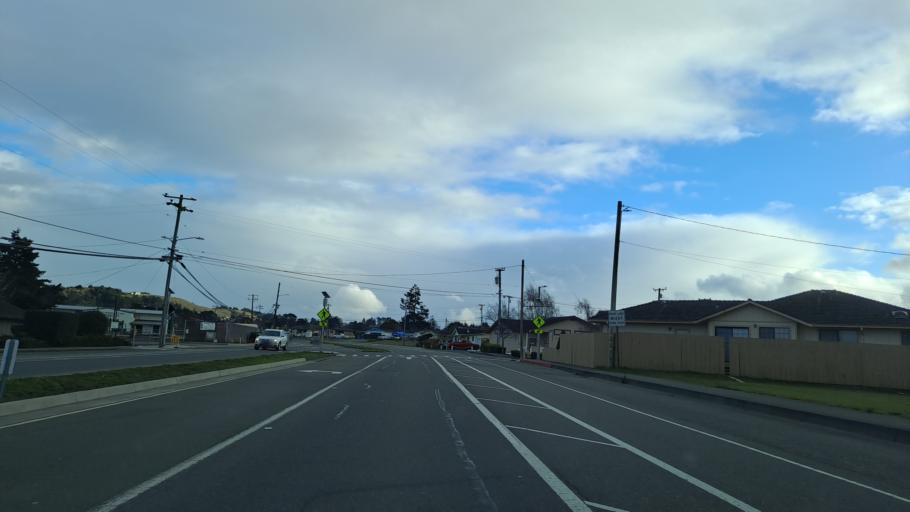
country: US
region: California
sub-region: Humboldt County
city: Fortuna
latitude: 40.5717
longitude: -124.1414
